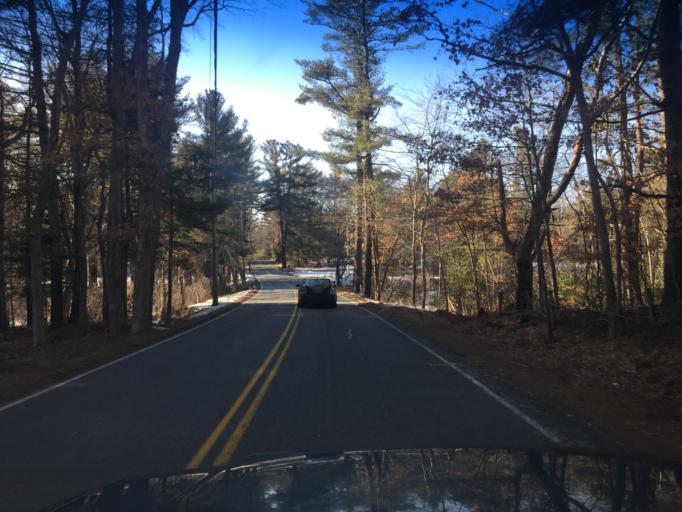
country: US
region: Massachusetts
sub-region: Norfolk County
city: Bellingham
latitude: 42.0912
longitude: -71.5116
